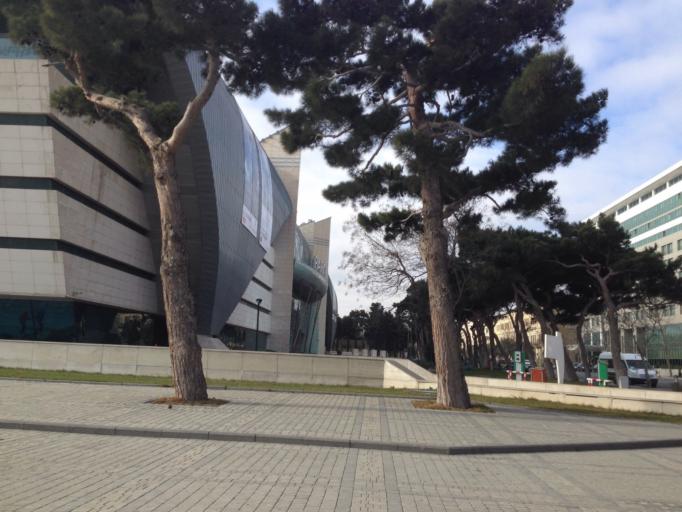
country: AZ
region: Baki
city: Baku
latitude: 40.3715
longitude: 49.8508
